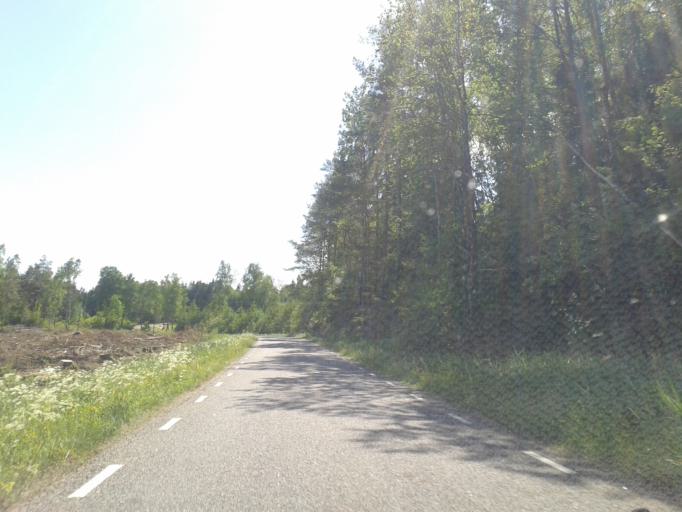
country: SE
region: Vaestra Goetaland
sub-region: Kungalvs Kommun
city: Diserod
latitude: 57.9883
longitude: 11.9557
